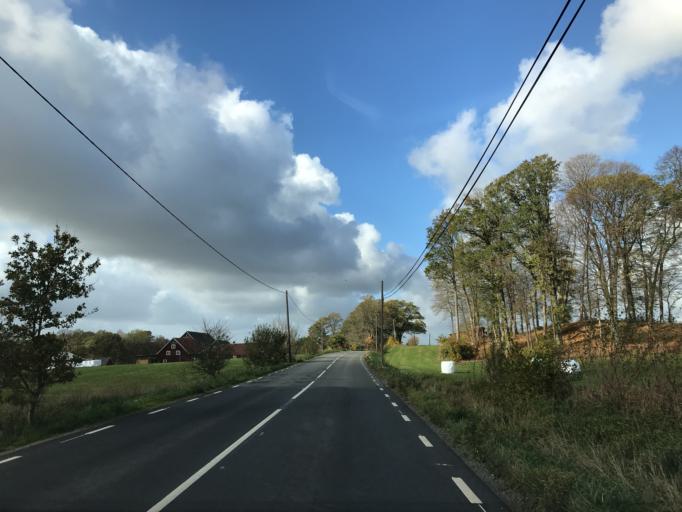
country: SE
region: Skane
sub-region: Perstorps Kommun
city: Perstorp
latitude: 56.0405
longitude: 13.3908
